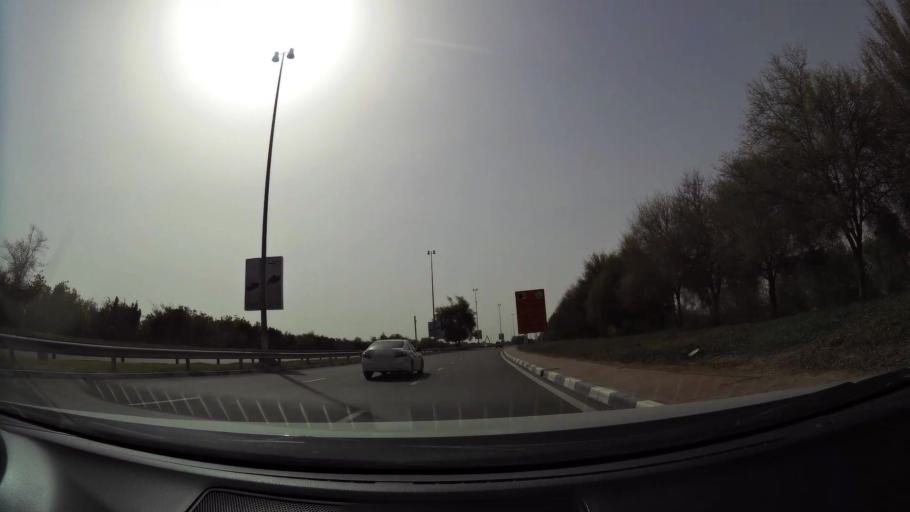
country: AE
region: Abu Dhabi
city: Al Ain
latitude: 24.1783
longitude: 55.6020
